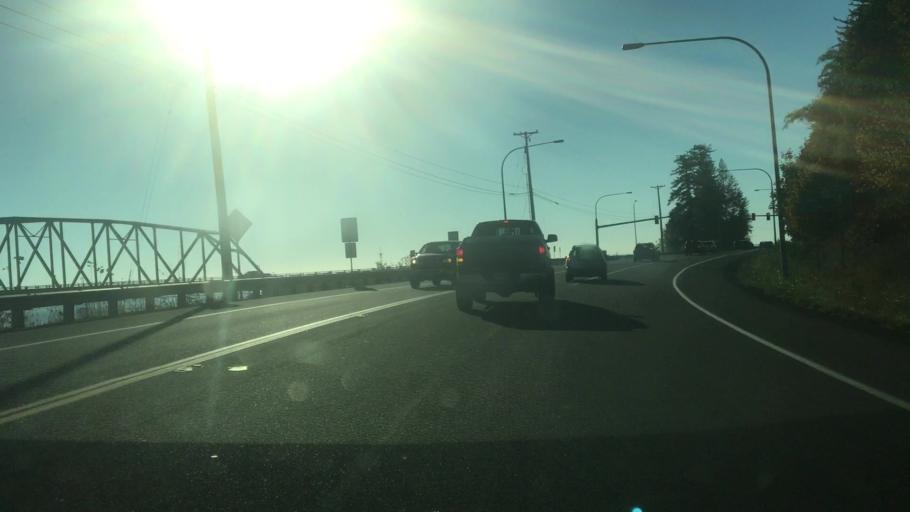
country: US
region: Oregon
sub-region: Clatsop County
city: Astoria
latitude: 46.2414
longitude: -123.8731
